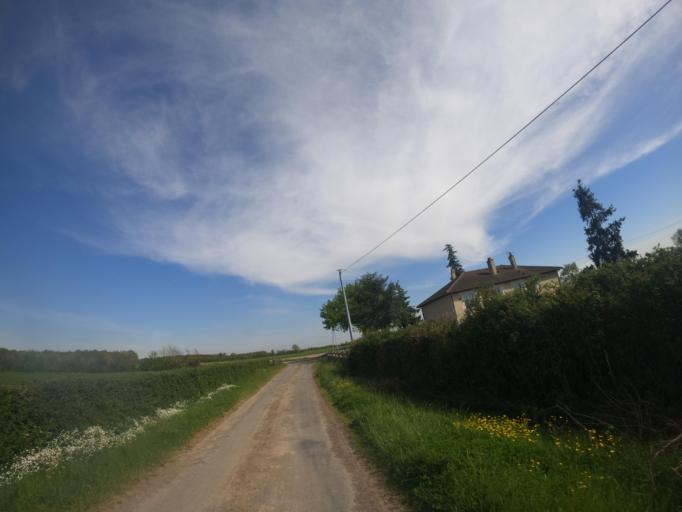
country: FR
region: Poitou-Charentes
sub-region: Departement des Deux-Sevres
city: Saint-Varent
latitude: 46.9247
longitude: -0.2402
